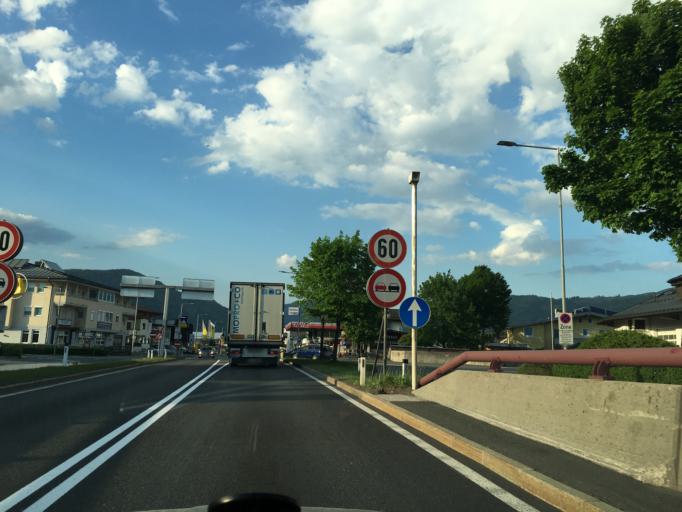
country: AT
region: Tyrol
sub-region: Politischer Bezirk Kitzbuhel
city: Sankt Johann in Tirol
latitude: 47.5251
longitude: 12.4232
